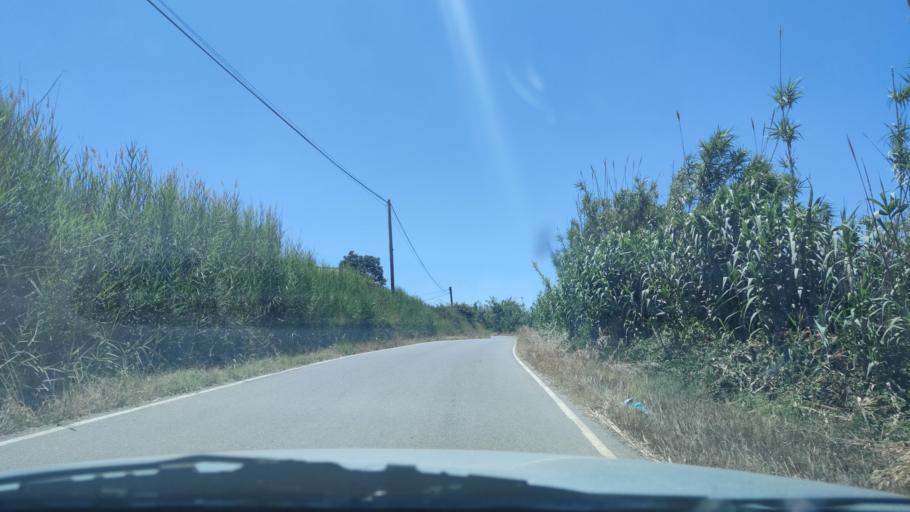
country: ES
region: Catalonia
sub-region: Provincia de Lleida
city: Alcoletge
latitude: 41.6379
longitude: 0.6591
